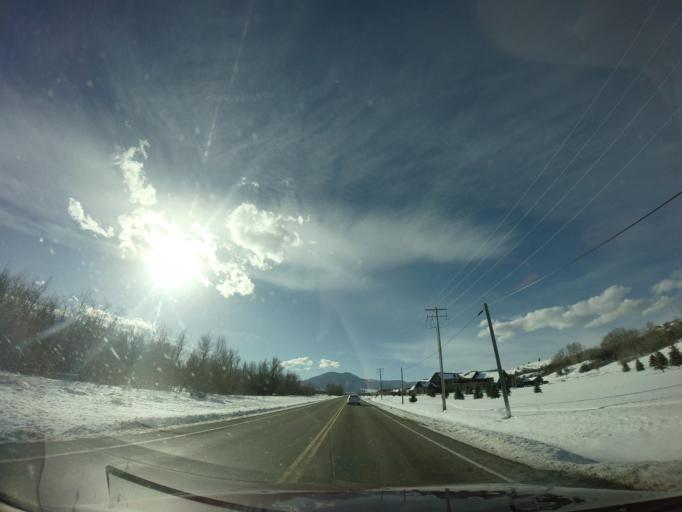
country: US
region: Montana
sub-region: Carbon County
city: Red Lodge
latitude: 45.2132
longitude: -109.2427
